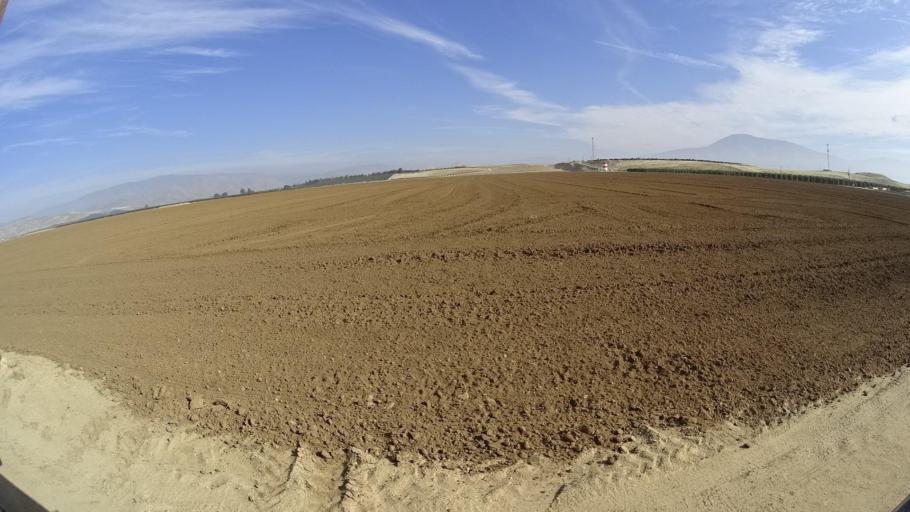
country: US
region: California
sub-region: Kern County
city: Arvin
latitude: 35.3133
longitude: -118.8074
